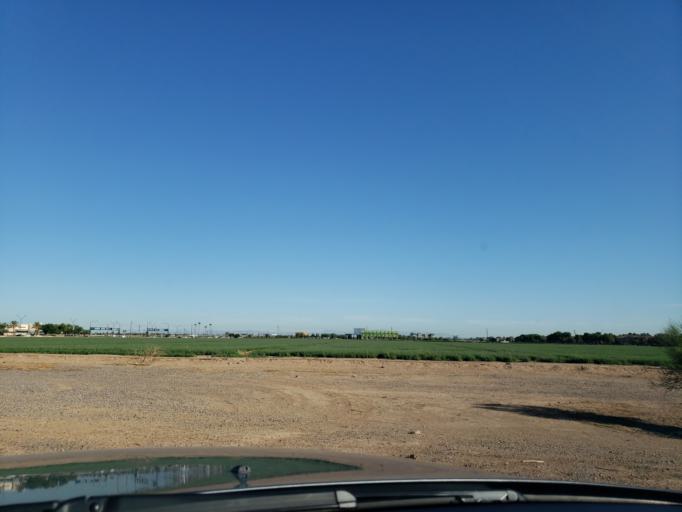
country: US
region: Arizona
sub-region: Maricopa County
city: Tolleson
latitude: 33.4458
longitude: -112.3042
